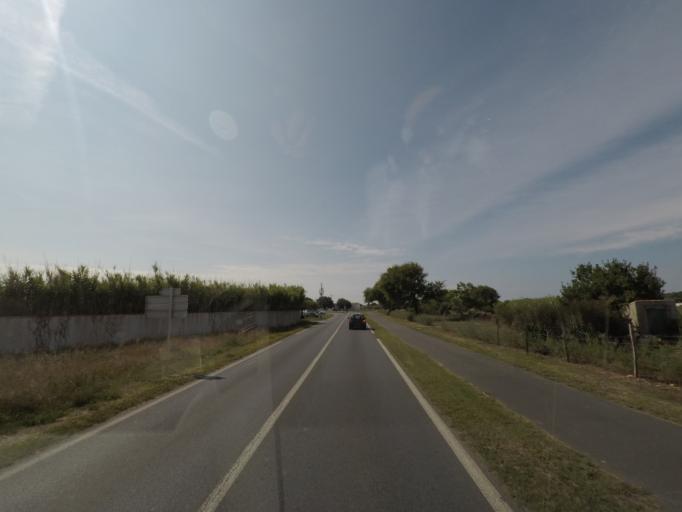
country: FR
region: Poitou-Charentes
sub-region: Departement de la Charente-Maritime
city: Ars-en-Re
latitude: 46.2087
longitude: -1.5217
